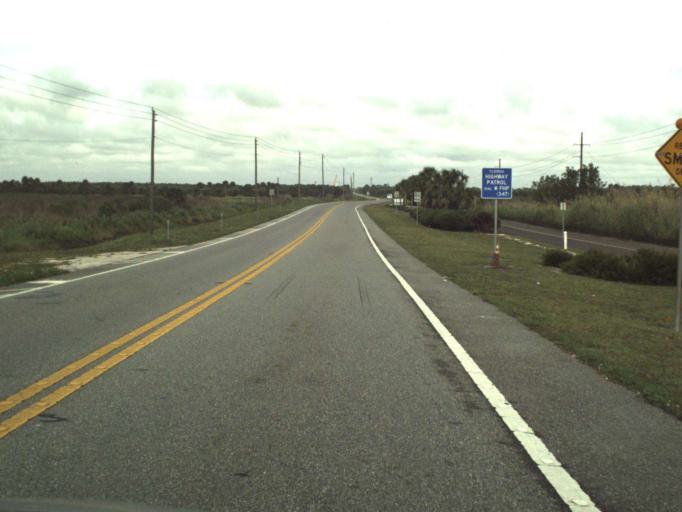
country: US
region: Florida
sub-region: Seminole County
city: Geneva
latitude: 28.7143
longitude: -81.0363
